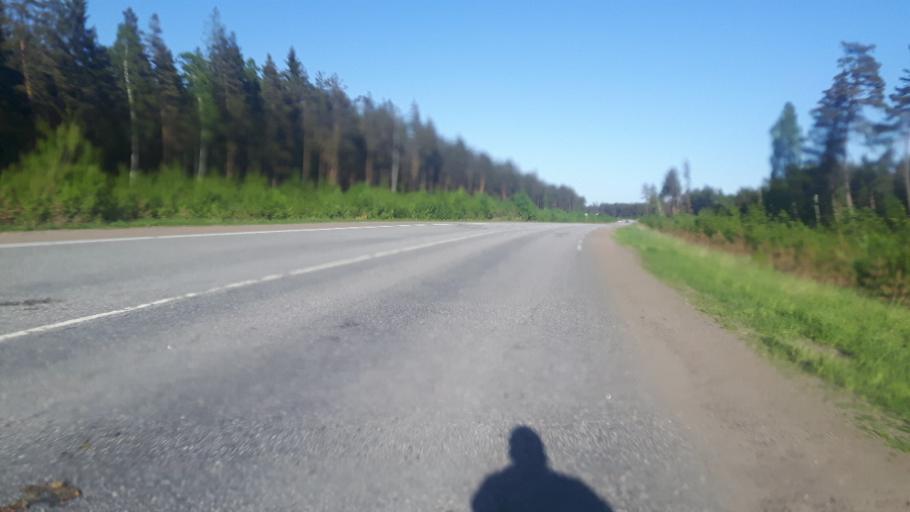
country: RU
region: Leningrad
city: Molodezhnoye
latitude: 60.1729
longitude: 29.2918
